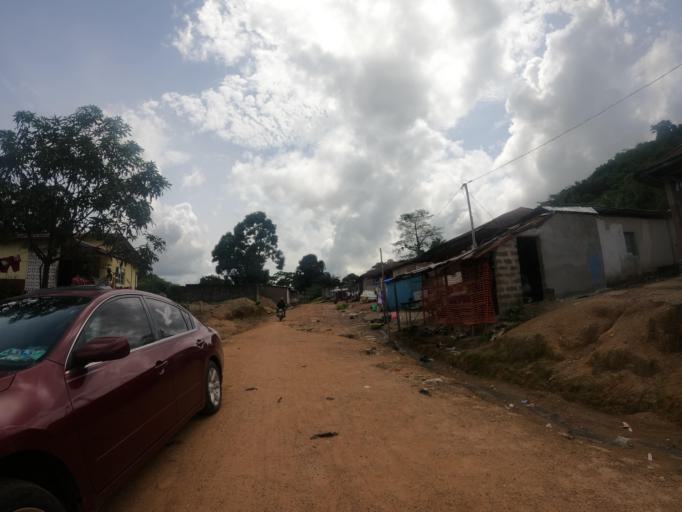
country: SL
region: Northern Province
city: Makeni
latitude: 8.8904
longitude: -12.0632
